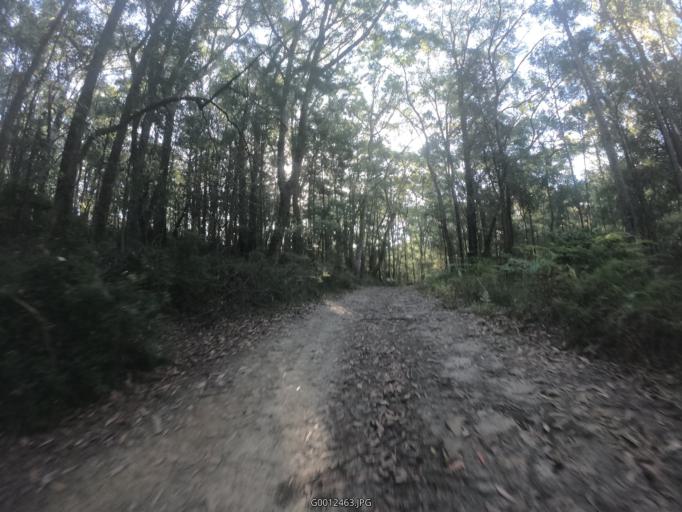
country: AU
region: New South Wales
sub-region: Lake Macquarie Shire
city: Cooranbong
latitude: -33.0857
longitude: 151.3582
